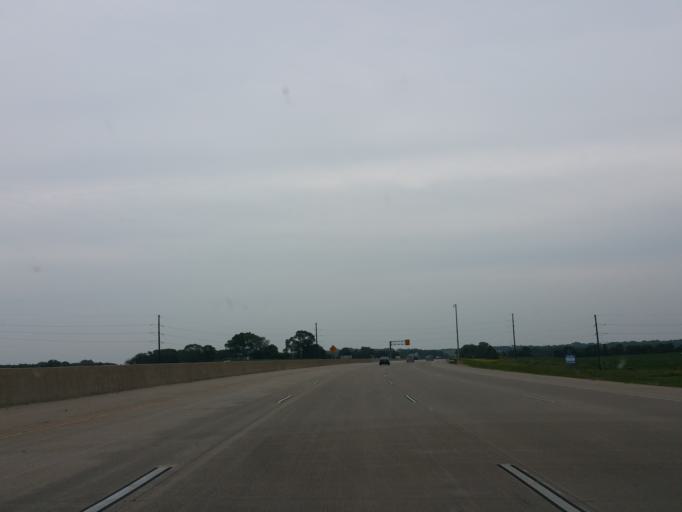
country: US
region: Wisconsin
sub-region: Dane County
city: Cottage Grove
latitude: 43.1034
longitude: -89.2698
